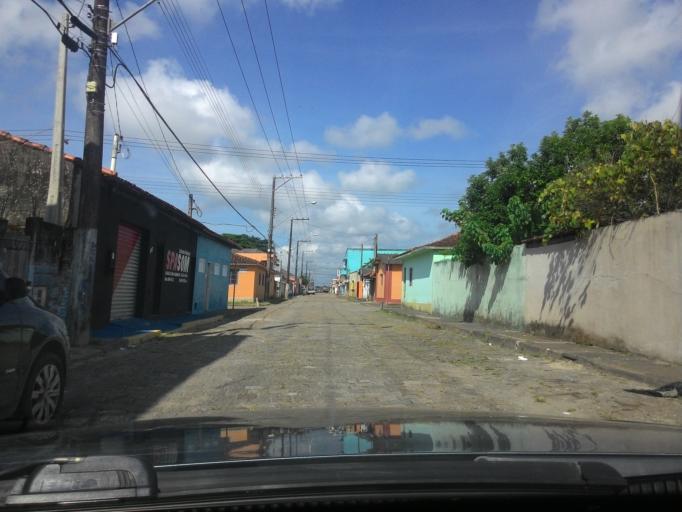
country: BR
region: Sao Paulo
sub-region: Iguape
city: Iguape
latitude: -24.7082
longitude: -47.5596
